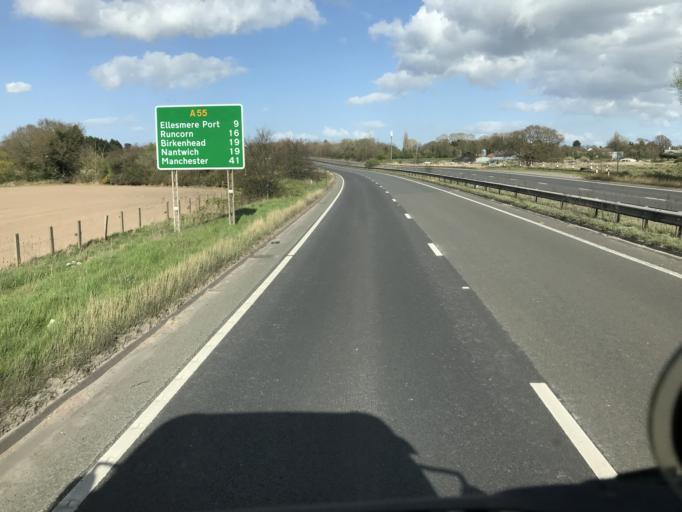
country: GB
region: England
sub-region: Cheshire West and Chester
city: Hoole
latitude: 53.1810
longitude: -2.8518
